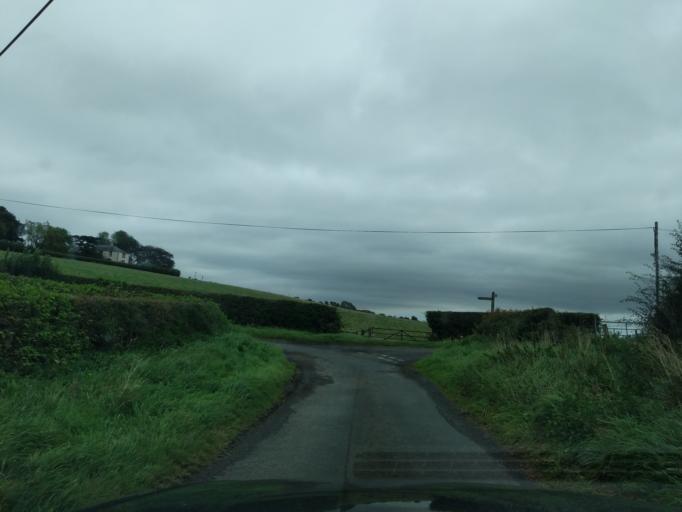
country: GB
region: Scotland
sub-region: The Scottish Borders
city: Kelso
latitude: 55.5960
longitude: -2.5171
